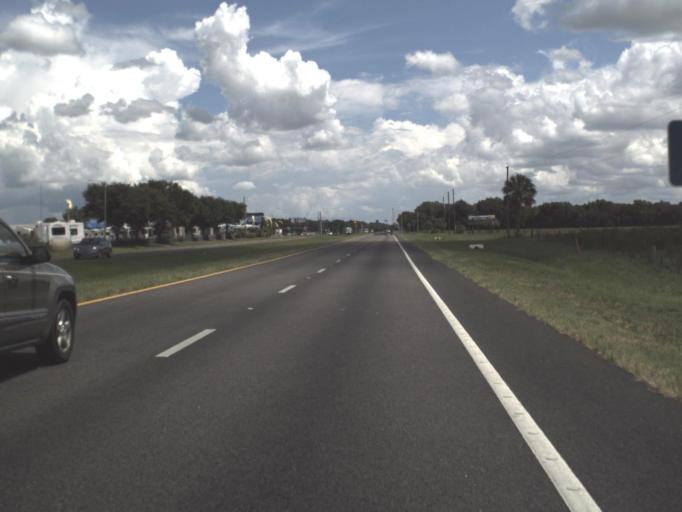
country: US
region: Florida
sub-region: Polk County
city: Wahneta
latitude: 27.9163
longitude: -81.7318
